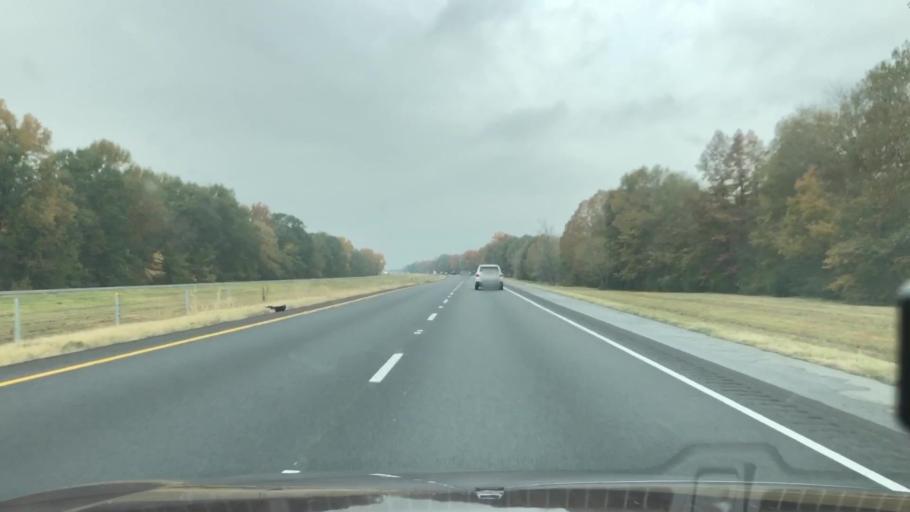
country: US
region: Louisiana
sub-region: Richland Parish
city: Rayville
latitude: 32.4658
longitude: -91.7986
